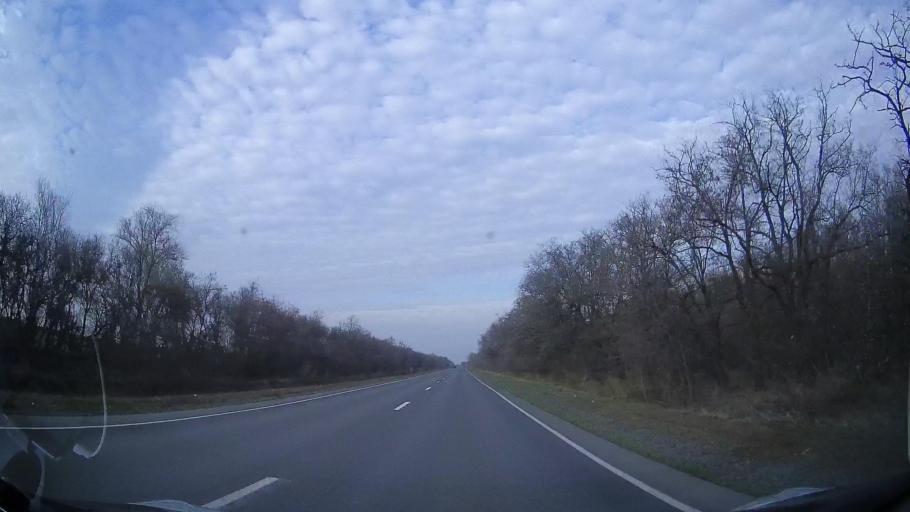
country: RU
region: Rostov
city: Bagayevskaya
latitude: 47.1277
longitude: 40.2767
